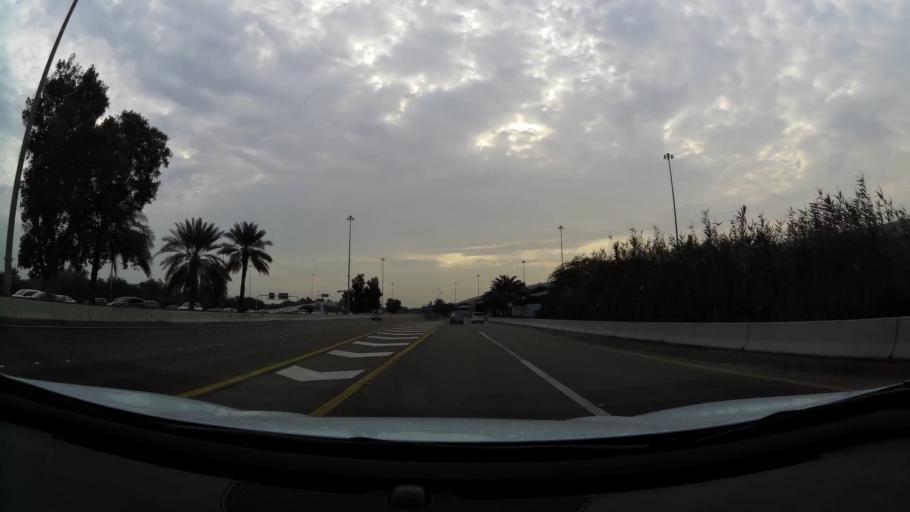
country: AE
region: Abu Dhabi
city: Abu Dhabi
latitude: 24.3911
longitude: 54.5295
